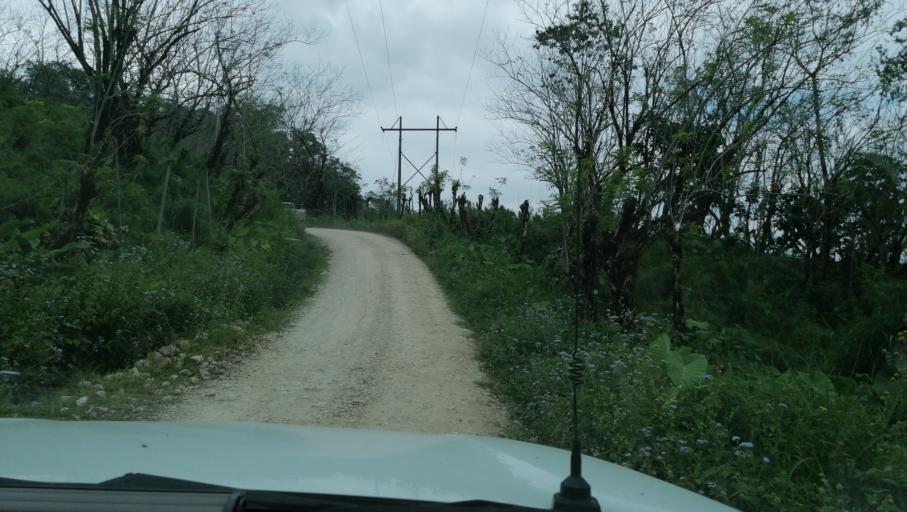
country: MX
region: Chiapas
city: Ocotepec
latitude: 17.2759
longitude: -93.2259
